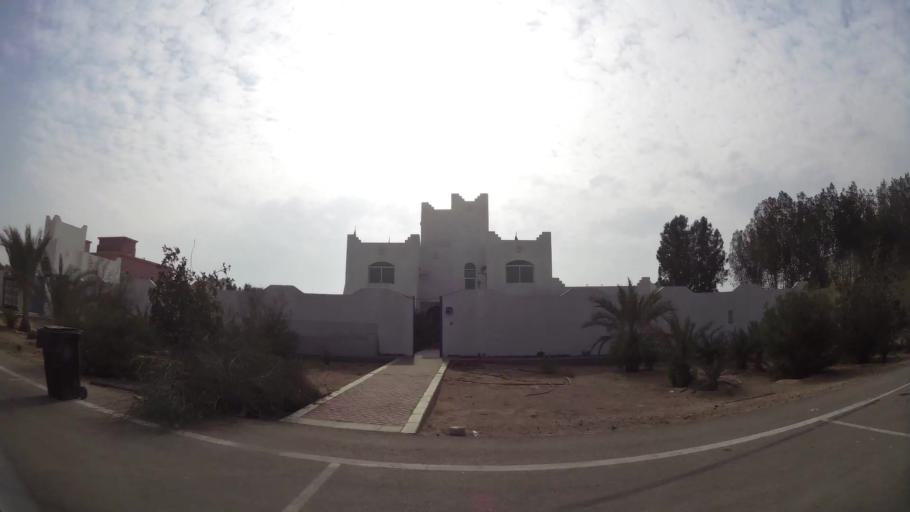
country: AE
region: Abu Dhabi
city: Abu Dhabi
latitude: 24.6693
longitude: 54.7737
